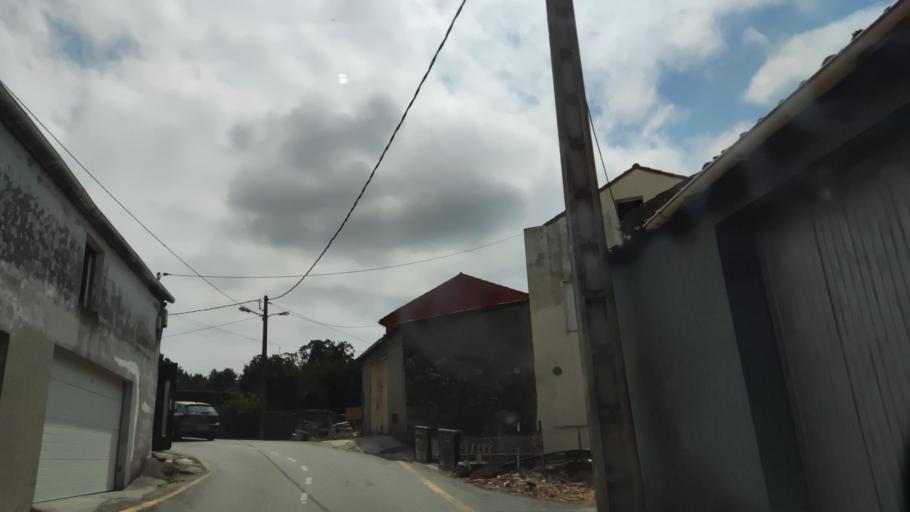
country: ES
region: Galicia
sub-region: Provincia da Coruna
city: Boiro
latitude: 42.6262
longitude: -8.8748
